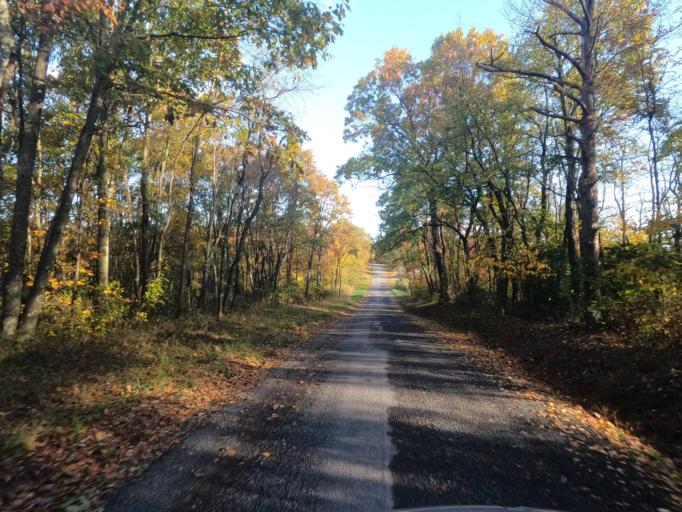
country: US
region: West Virginia
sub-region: Morgan County
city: Berkeley Springs
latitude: 39.6171
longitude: -78.4894
